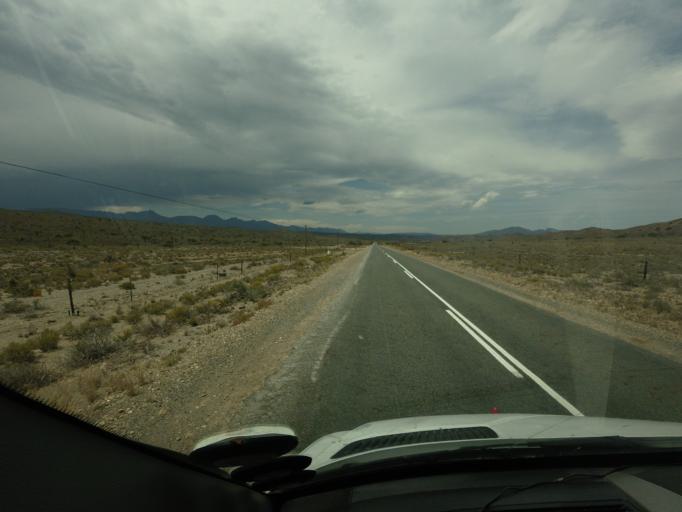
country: ZA
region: Western Cape
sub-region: Eden District Municipality
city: Ladismith
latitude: -33.6045
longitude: 21.0767
